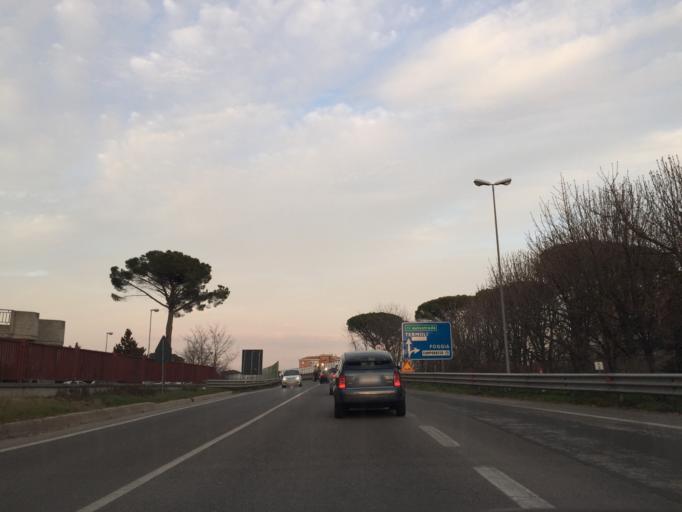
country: IT
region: Molise
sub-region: Provincia di Campobasso
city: Campobasso
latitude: 41.5570
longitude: 14.6731
